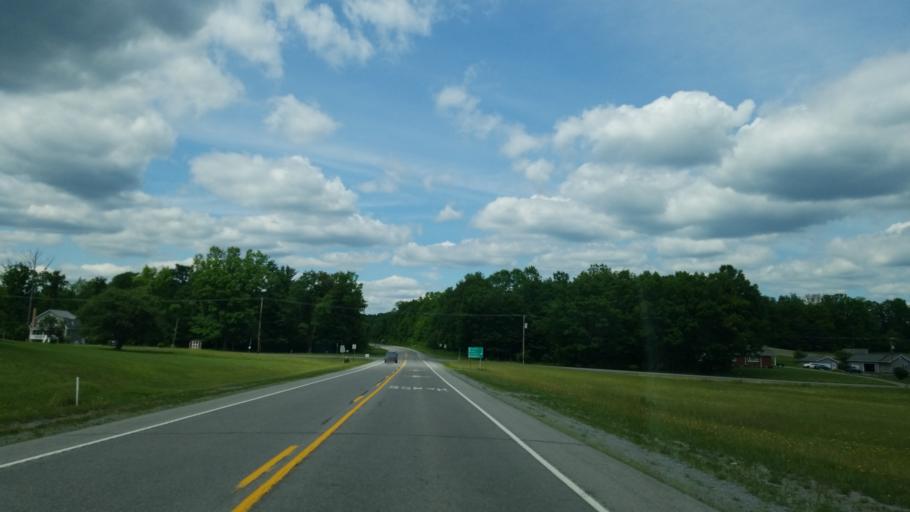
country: US
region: Pennsylvania
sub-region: Clearfield County
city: Osceola Mills
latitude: 40.8964
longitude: -78.3825
